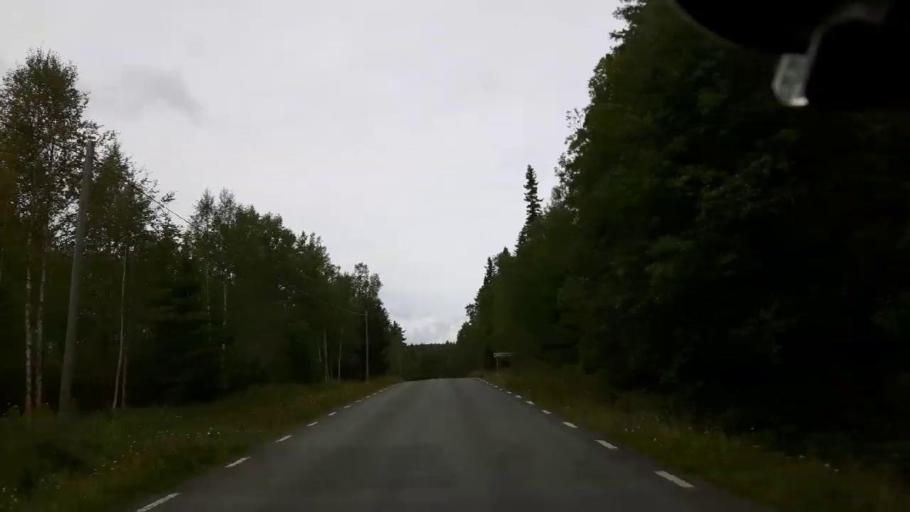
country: SE
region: Jaemtland
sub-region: Krokoms Kommun
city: Valla
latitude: 63.4709
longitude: 14.0663
